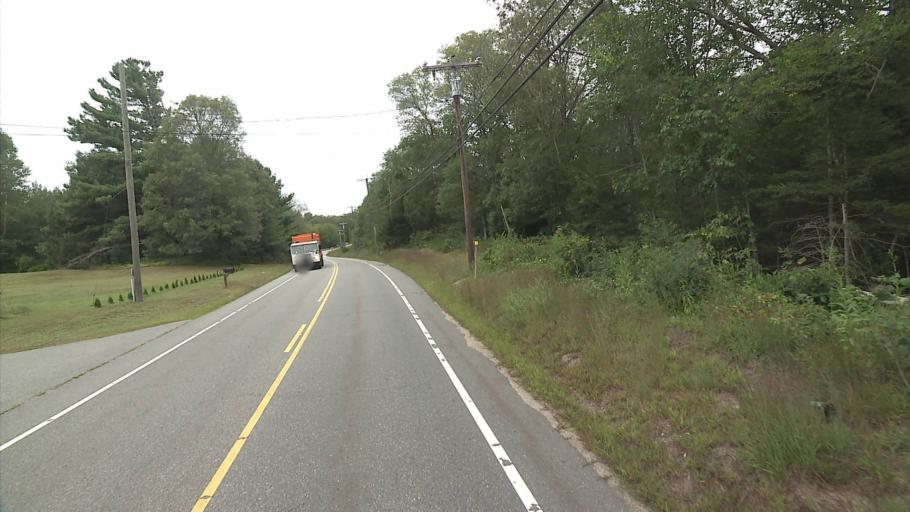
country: US
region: Connecticut
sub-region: New London County
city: Colchester
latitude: 41.6170
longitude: -72.3439
